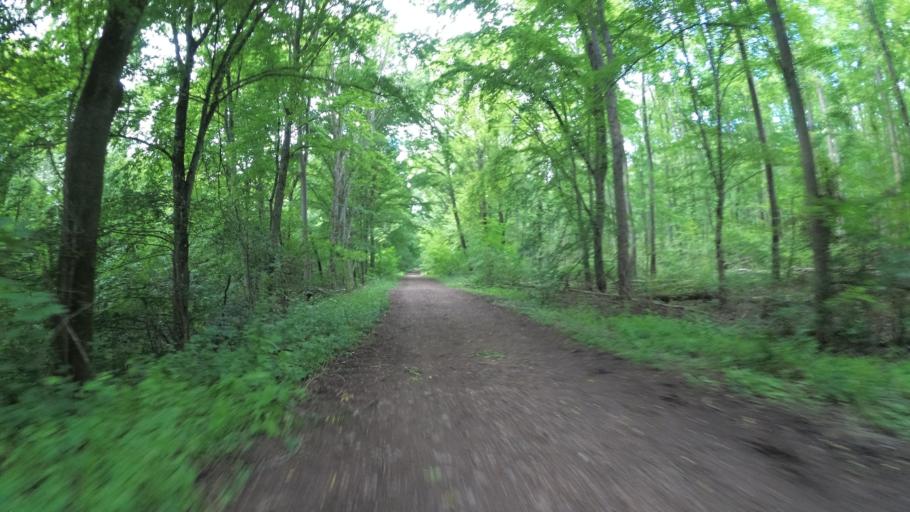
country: DE
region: Saarland
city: Puttlingen
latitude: 49.2672
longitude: 6.8786
